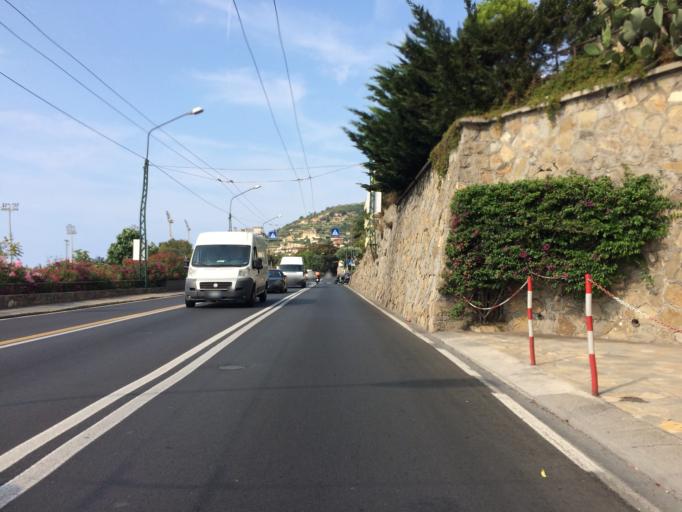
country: IT
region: Liguria
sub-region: Provincia di Imperia
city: San Remo
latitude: 43.8065
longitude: 7.7503
